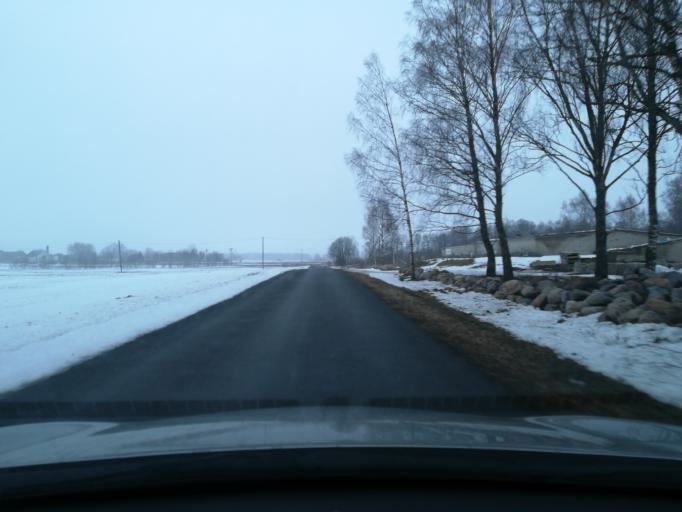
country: EE
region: Harju
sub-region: Raasiku vald
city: Raasiku
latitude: 59.3526
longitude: 25.2063
